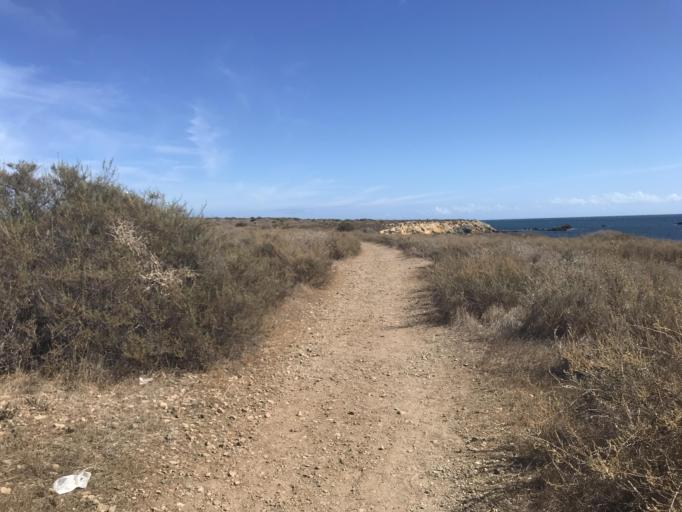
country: ES
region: Valencia
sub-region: Provincia de Alicante
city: Santa Pola
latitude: 38.1633
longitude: -0.4750
